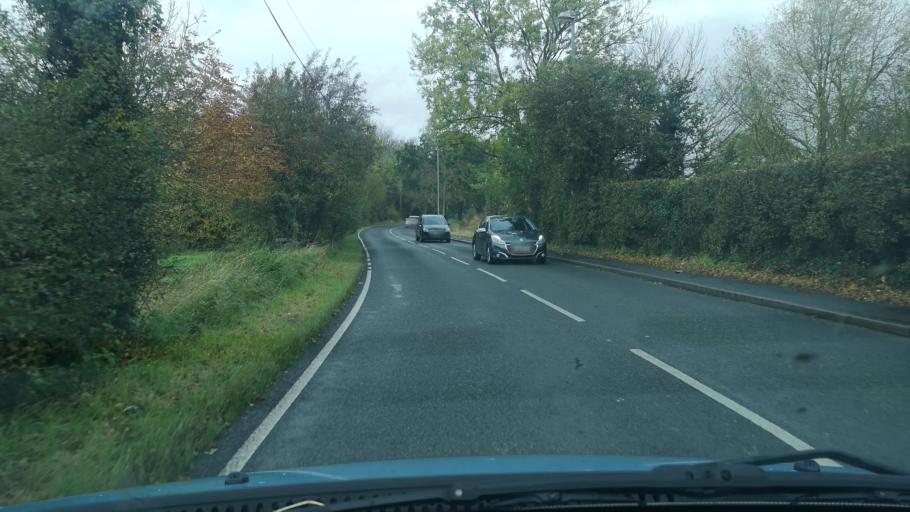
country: GB
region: England
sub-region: City and Borough of Wakefield
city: Low Ackworth
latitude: 53.6588
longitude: -1.3391
